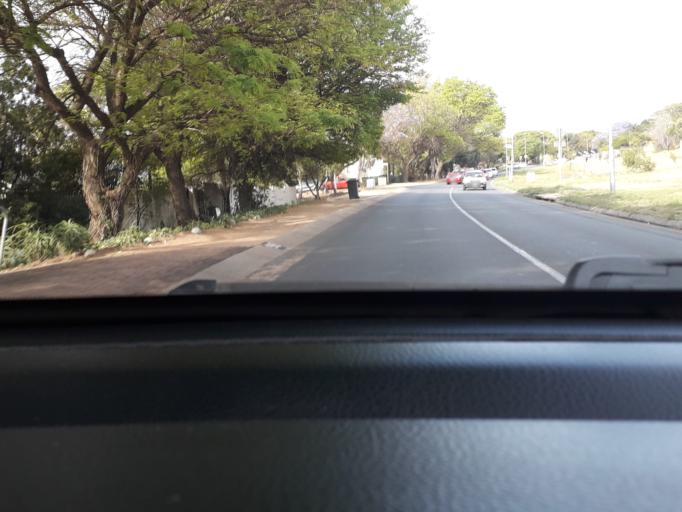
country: ZA
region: Gauteng
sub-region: City of Johannesburg Metropolitan Municipality
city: Diepsloot
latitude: -26.0342
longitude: 28.0030
